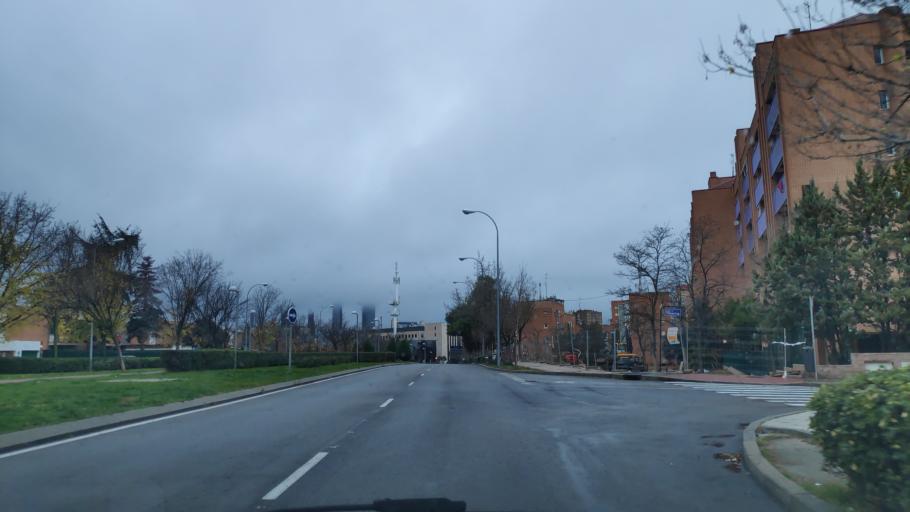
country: ES
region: Madrid
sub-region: Provincia de Madrid
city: Pinar de Chamartin
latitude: 40.4719
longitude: -3.6601
